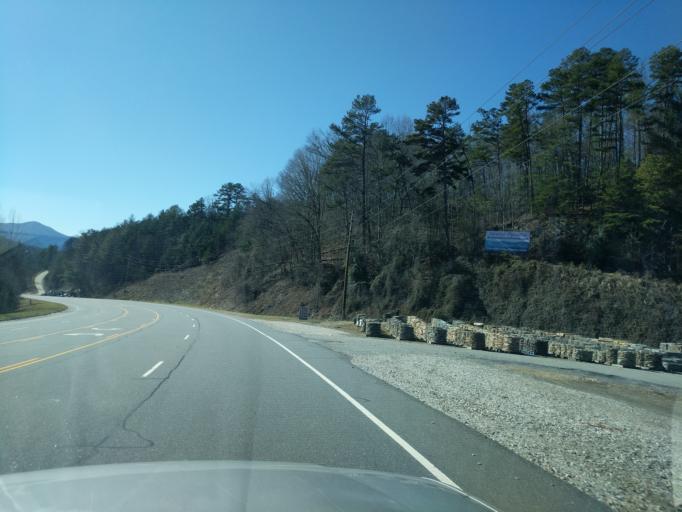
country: US
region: North Carolina
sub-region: Swain County
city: Bryson City
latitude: 35.3741
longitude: -83.5379
